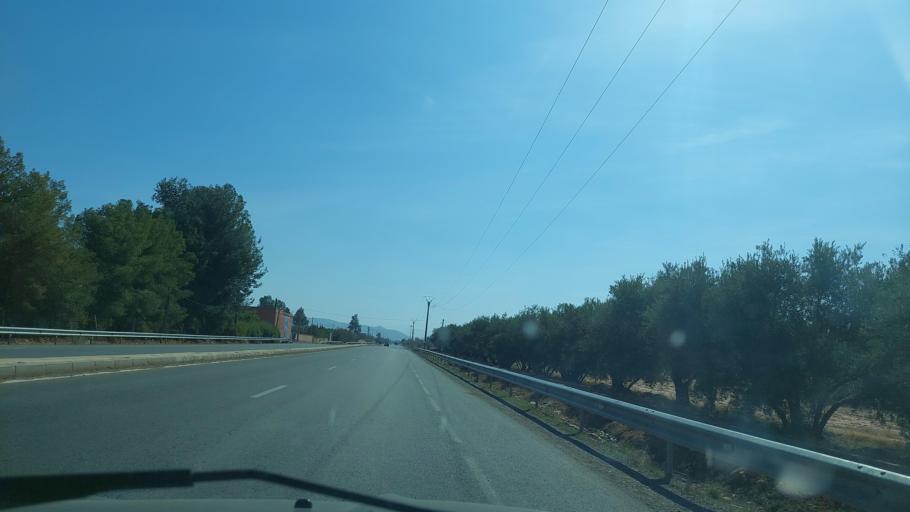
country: MA
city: Sidi Abdallah Ghiat
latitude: 31.5651
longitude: -7.7202
